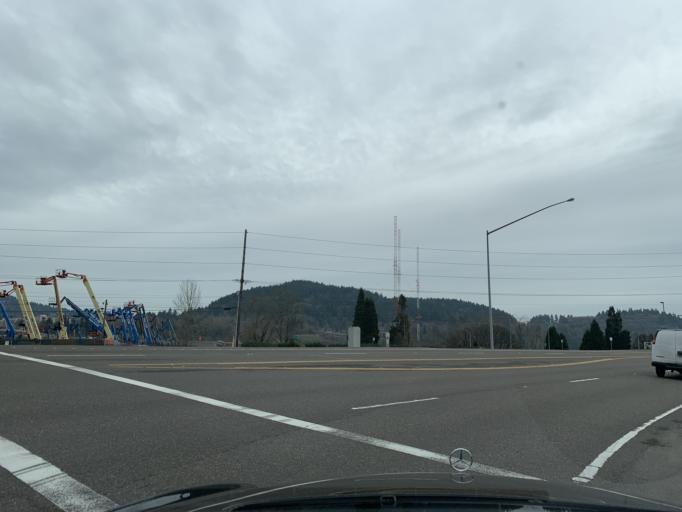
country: US
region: Oregon
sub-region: Clackamas County
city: Clackamas
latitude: 45.4215
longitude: -122.5745
